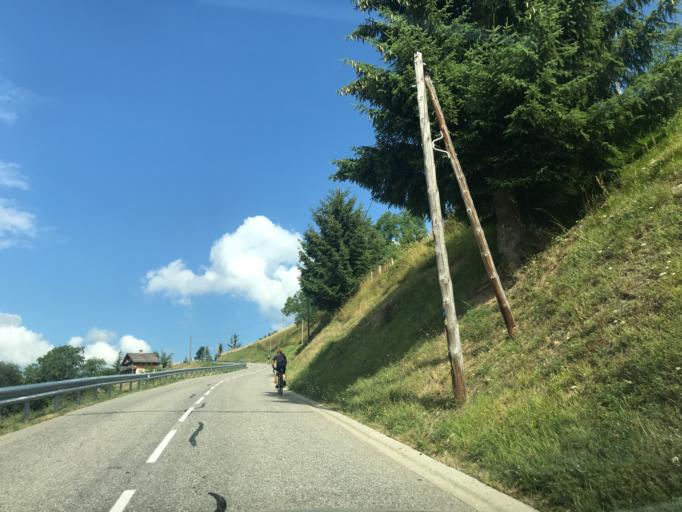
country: FR
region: Rhone-Alpes
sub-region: Departement de la Haute-Savoie
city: Thones
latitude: 45.8639
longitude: 6.3786
